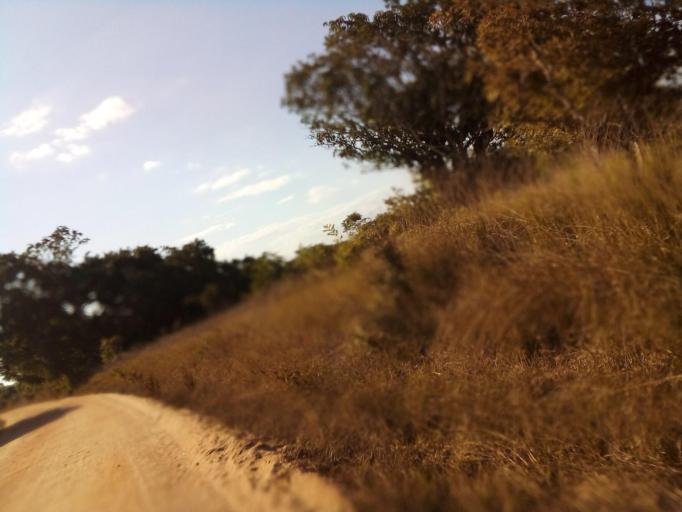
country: MZ
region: Zambezia
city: Quelimane
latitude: -17.5440
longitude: 36.6271
